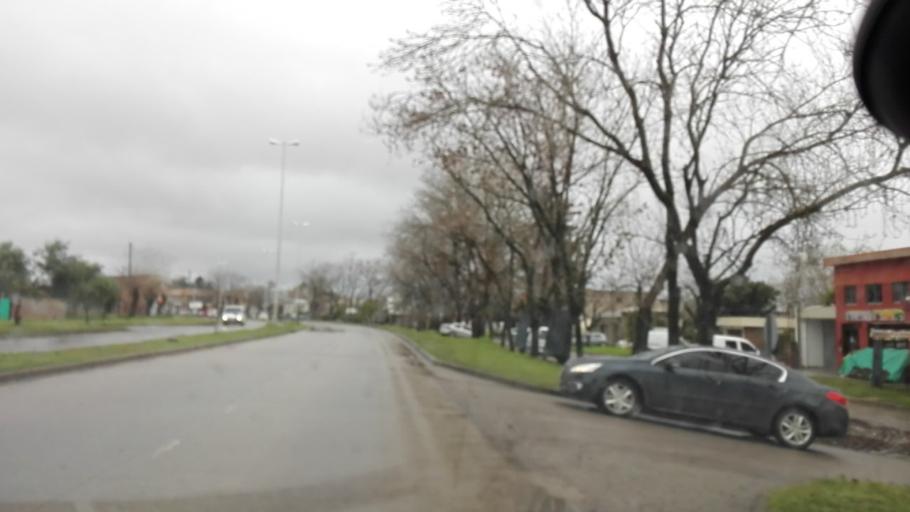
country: AR
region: Buenos Aires
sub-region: Partido de Brandsen
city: Brandsen
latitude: -35.1752
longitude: -58.2366
